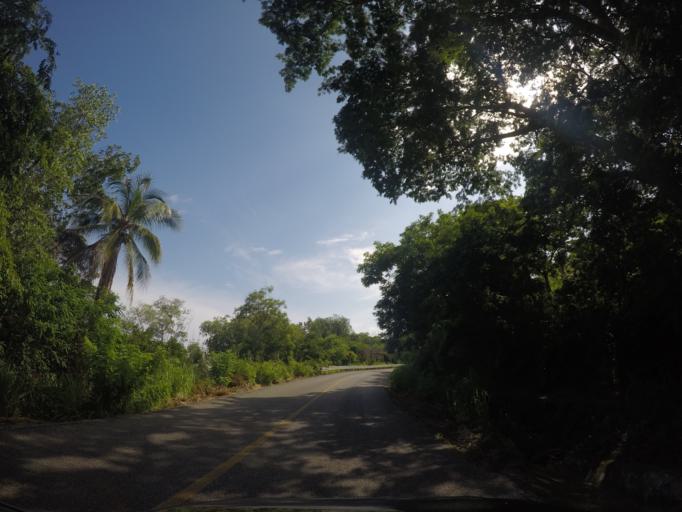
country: MX
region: Oaxaca
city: San Pedro Mixtepec
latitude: 15.9399
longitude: -97.1677
